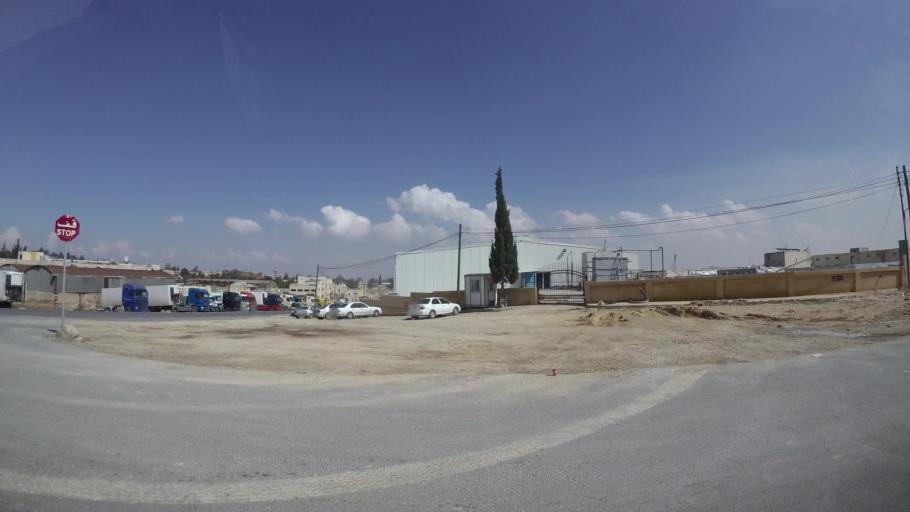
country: JO
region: Zarqa
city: Russeifa
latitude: 31.9940
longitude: 36.0065
